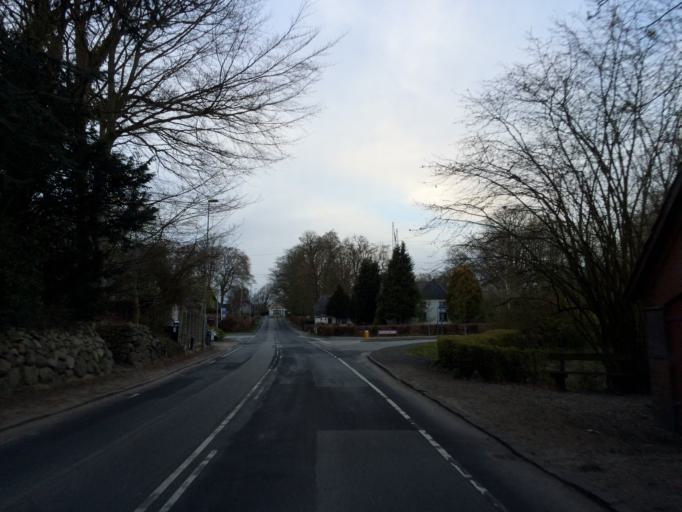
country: DK
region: South Denmark
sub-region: Odense Kommune
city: Bellinge
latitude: 55.3781
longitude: 10.2657
